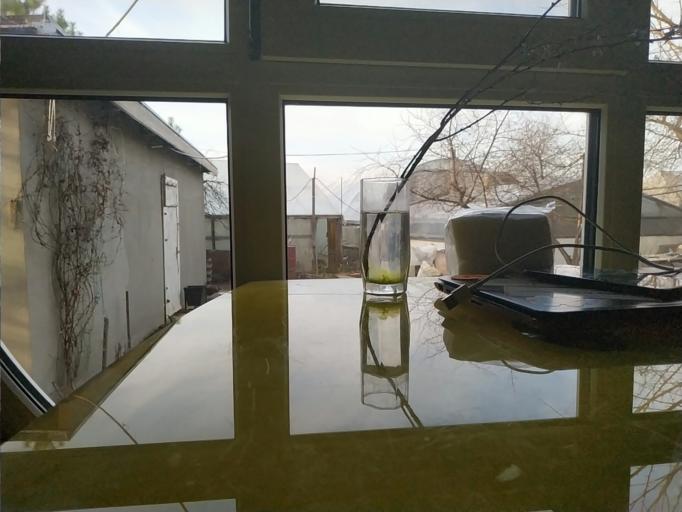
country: RU
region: Republic of Karelia
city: Suoyarvi
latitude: 62.0156
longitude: 32.2025
